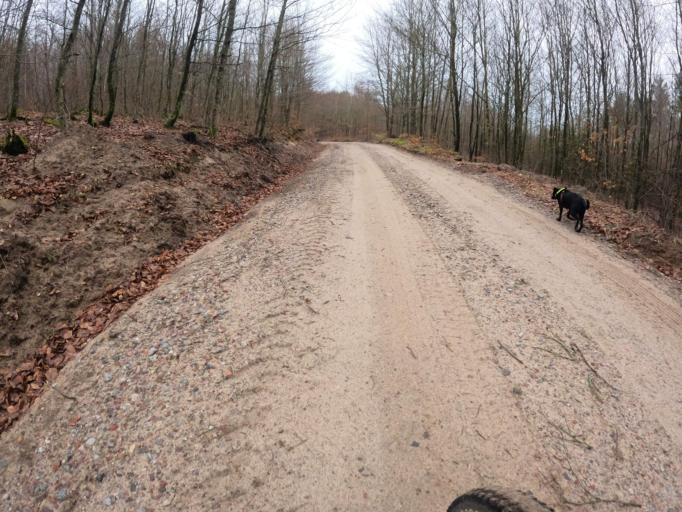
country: PL
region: West Pomeranian Voivodeship
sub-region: Powiat koszalinski
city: Polanow
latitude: 54.2321
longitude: 16.6779
